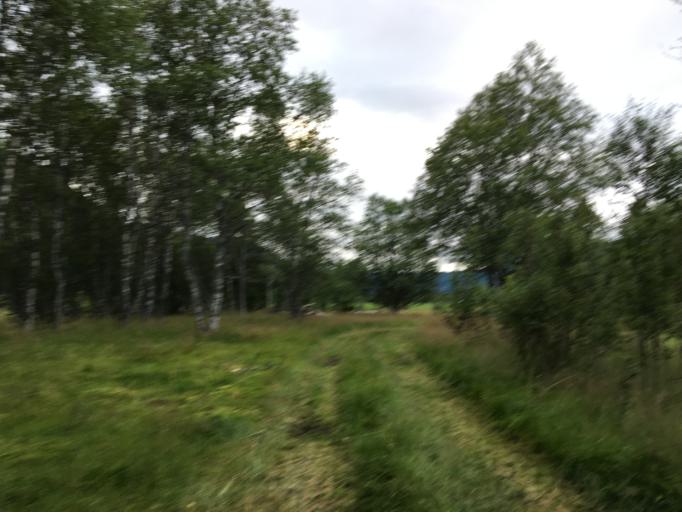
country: NO
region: Buskerud
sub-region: Hol
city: Hol
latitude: 60.6162
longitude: 8.2257
